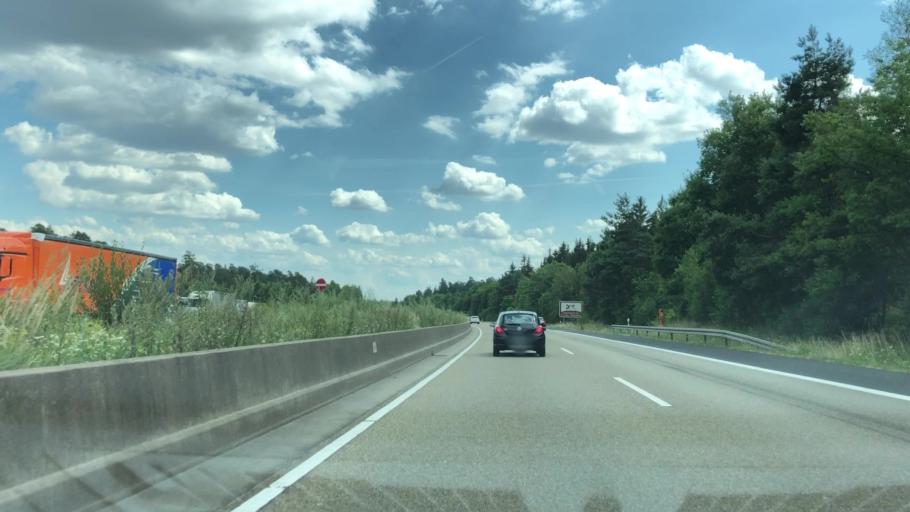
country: DE
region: Hesse
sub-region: Regierungsbezirk Kassel
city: Petersberg
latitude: 50.6258
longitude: 9.6761
